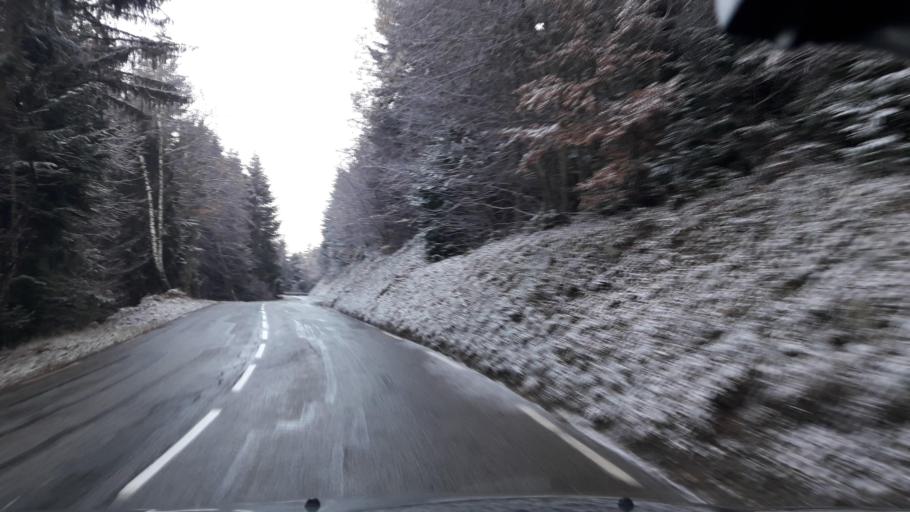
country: FR
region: Rhone-Alpes
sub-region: Departement de l'Isere
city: Allevard
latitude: 45.3910
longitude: 6.0900
